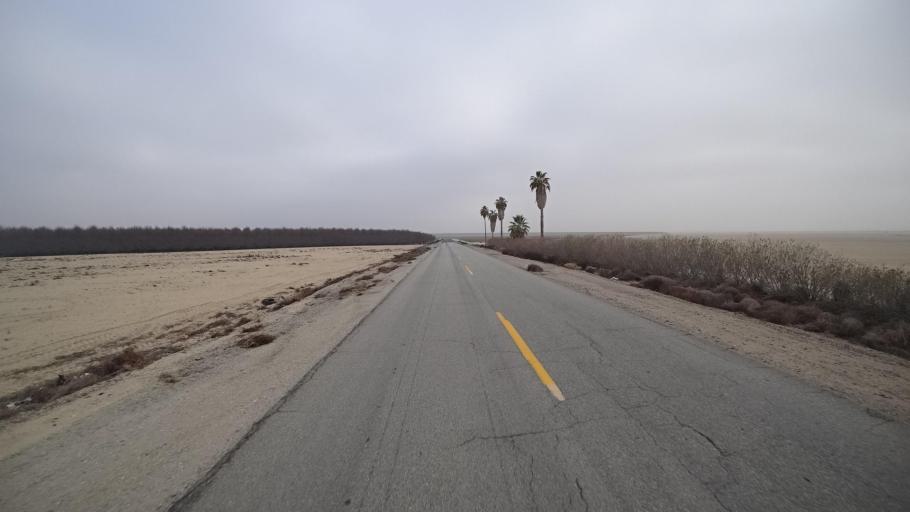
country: US
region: California
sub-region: Kern County
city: Maricopa
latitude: 35.1221
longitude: -119.3602
